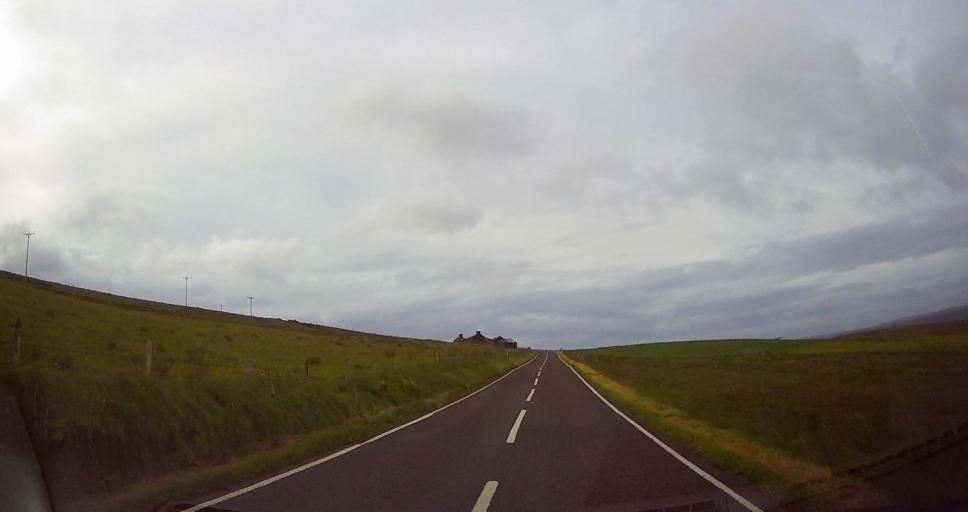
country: GB
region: Scotland
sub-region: Orkney Islands
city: Stromness
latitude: 58.9247
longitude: -3.1991
